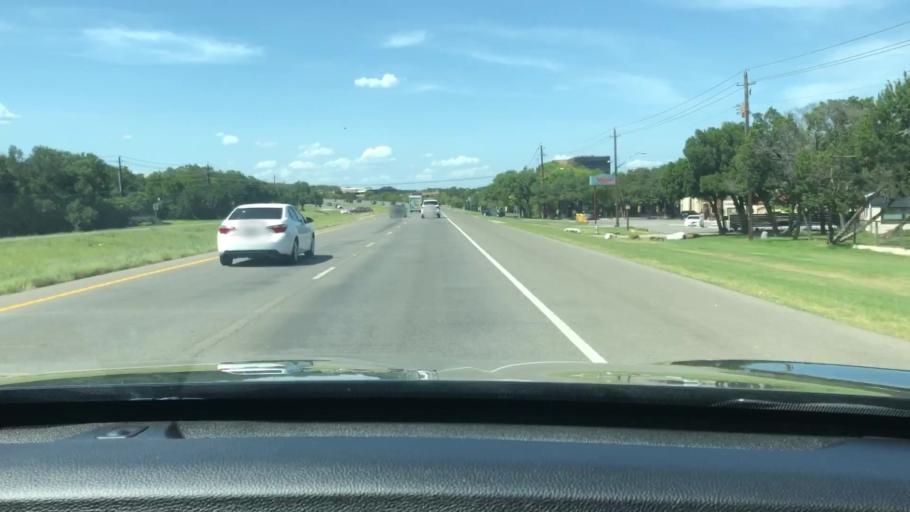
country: US
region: Texas
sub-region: Travis County
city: Rollingwood
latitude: 30.2698
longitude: -97.8177
